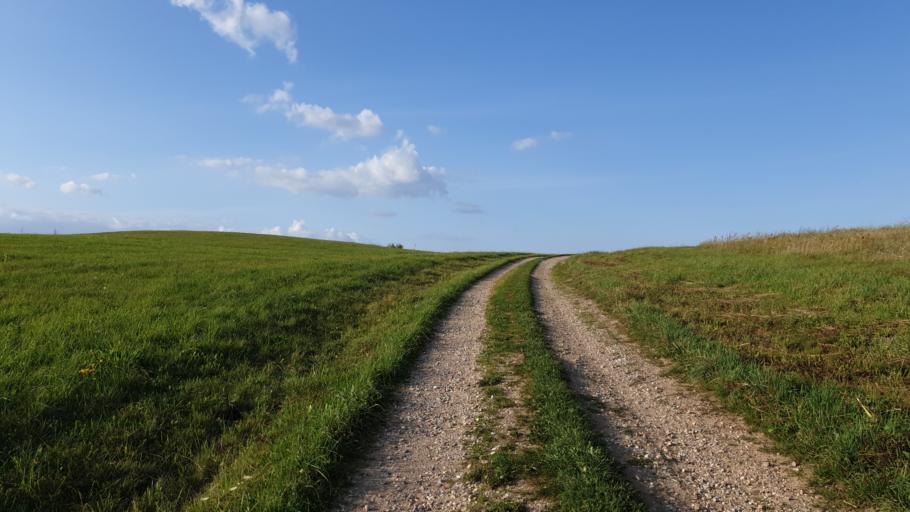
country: LT
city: Grigiskes
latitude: 54.7712
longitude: 25.0310
